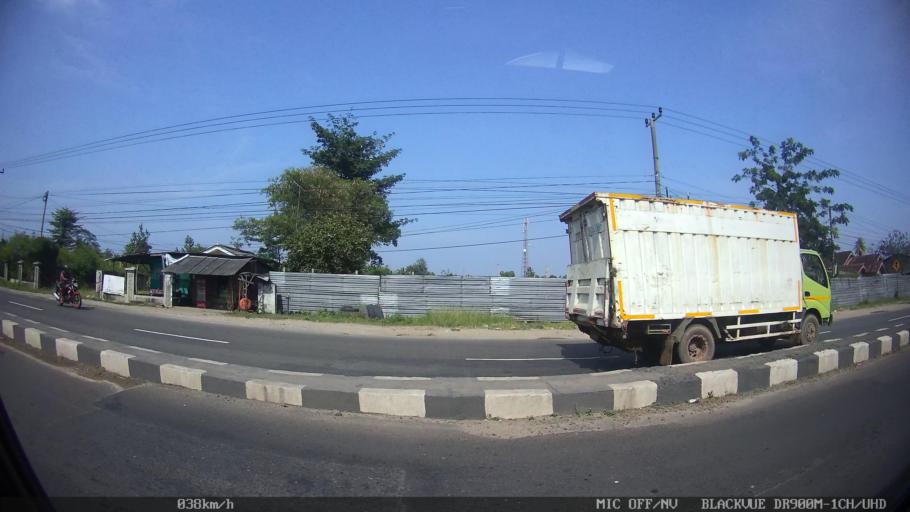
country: ID
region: Lampung
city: Natar
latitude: -5.2556
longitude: 105.1831
